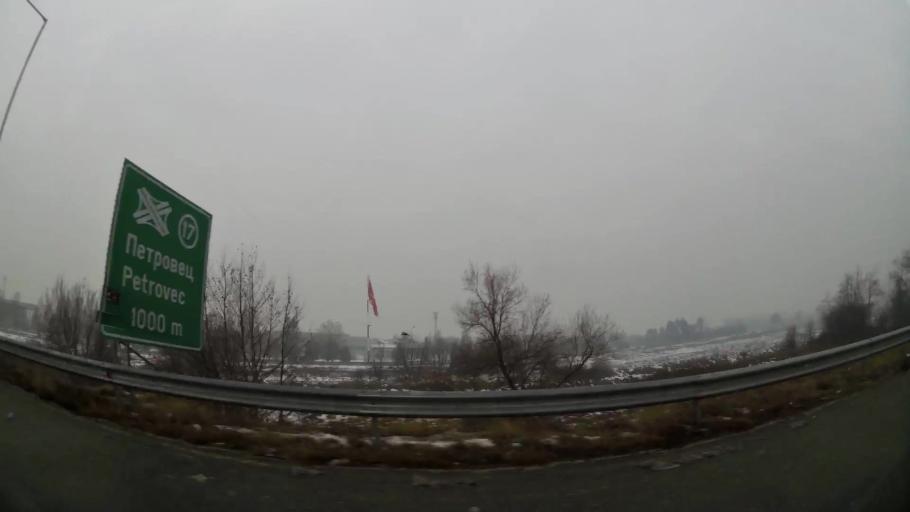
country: MK
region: Petrovec
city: Petrovec
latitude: 41.9567
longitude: 21.6309
